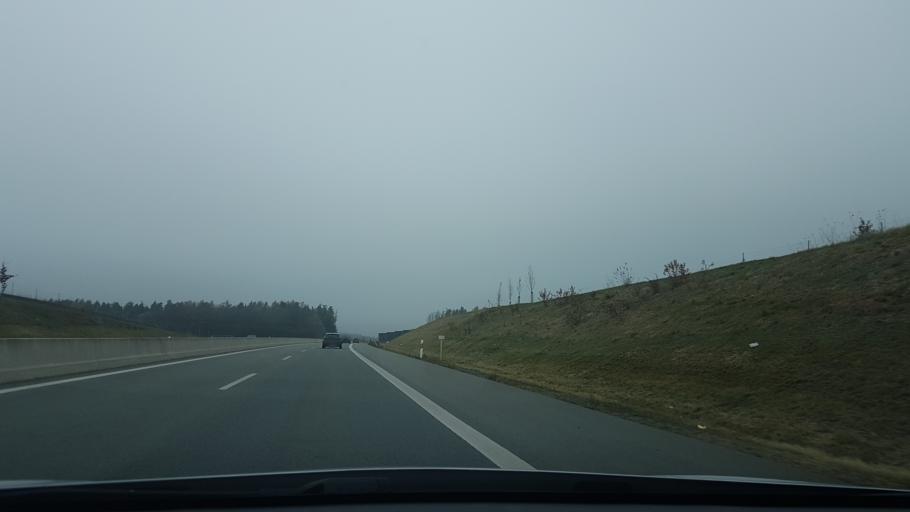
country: DE
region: Bavaria
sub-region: Lower Bavaria
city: Ergoldsbach
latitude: 48.6920
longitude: 12.1811
